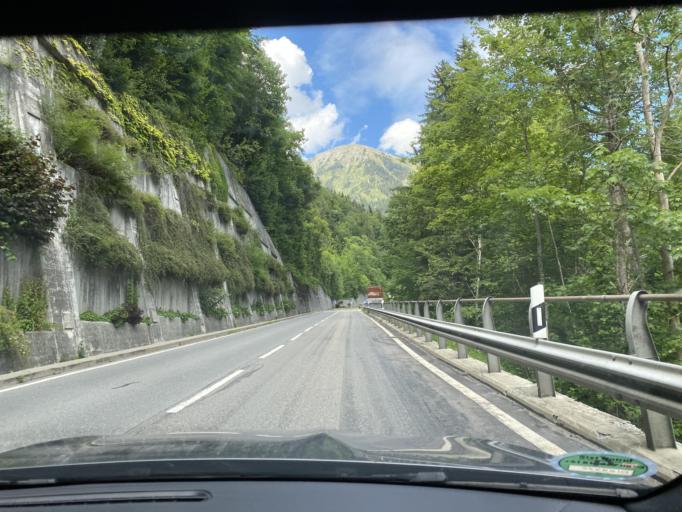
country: CH
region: Vaud
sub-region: Aigle District
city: Leysin
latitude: 46.3595
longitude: 7.0487
